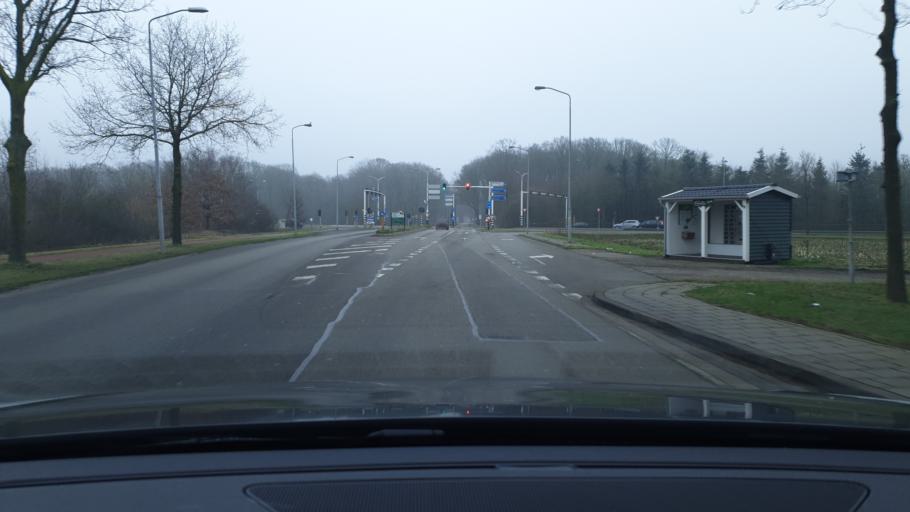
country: NL
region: North Brabant
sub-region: Gemeente Eindhoven
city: Meerhoven
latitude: 51.4645
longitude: 5.4164
